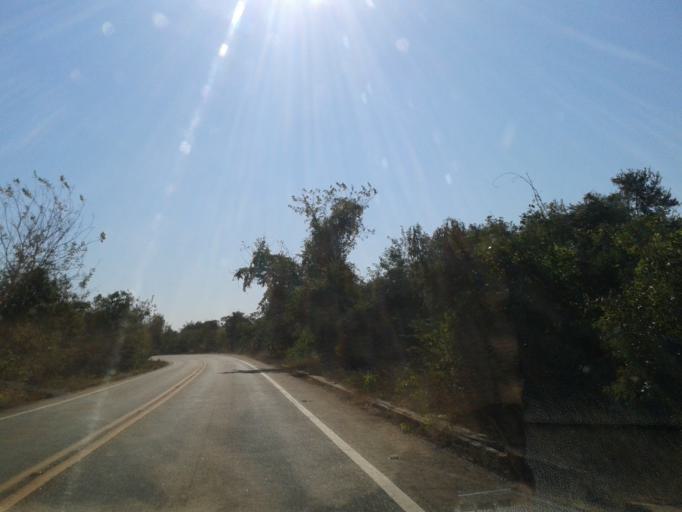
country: BR
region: Goias
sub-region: Mozarlandia
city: Mozarlandia
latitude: -14.6523
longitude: -50.5223
